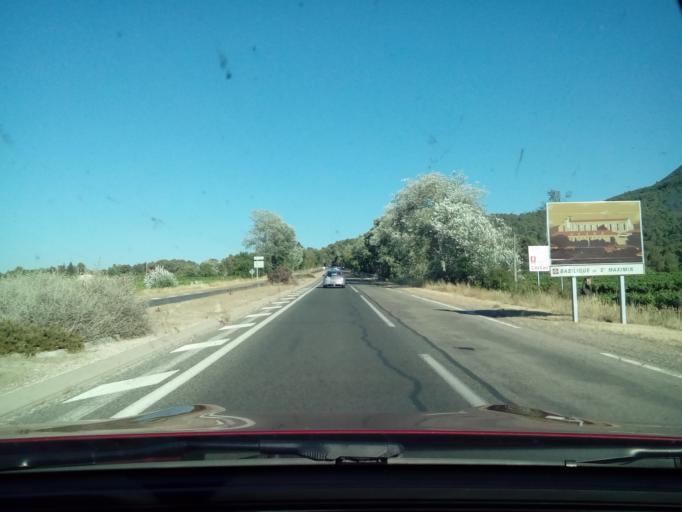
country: FR
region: Provence-Alpes-Cote d'Azur
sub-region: Departement du Var
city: Pourrieres
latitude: 43.4735
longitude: 5.7665
